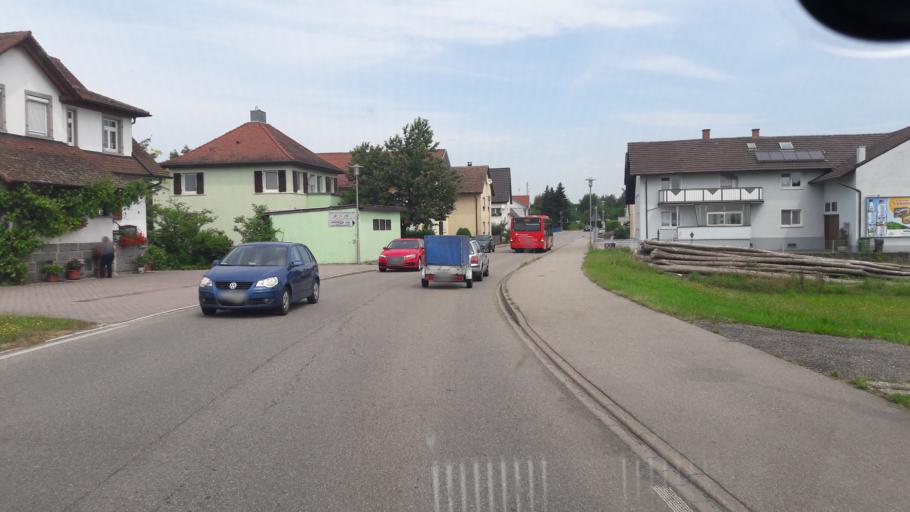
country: DE
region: Baden-Wuerttemberg
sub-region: Freiburg Region
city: Appenweier
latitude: 48.5558
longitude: 7.9797
